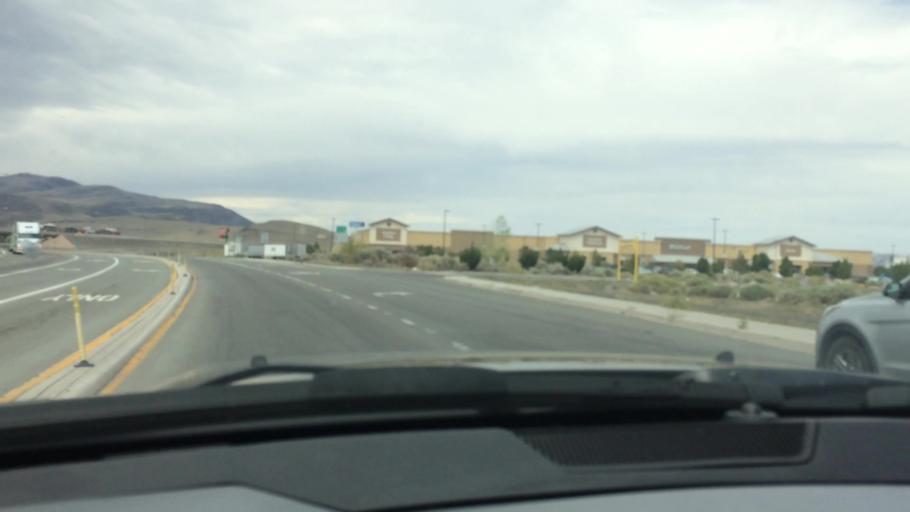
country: US
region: Nevada
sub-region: Lyon County
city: Fernley
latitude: 39.6097
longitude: -119.2197
